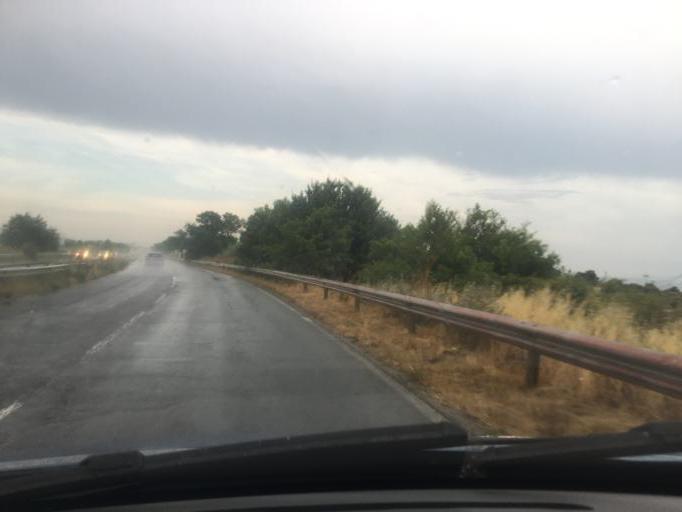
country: BG
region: Burgas
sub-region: Obshtina Burgas
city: Burgas
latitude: 42.5628
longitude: 27.5377
